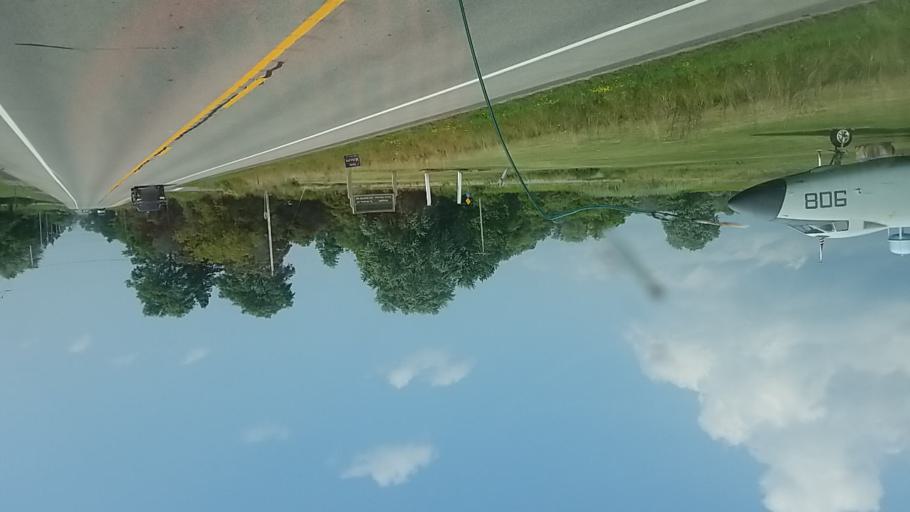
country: US
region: New York
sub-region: Fulton County
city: Johnstown
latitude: 42.9938
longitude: -74.3380
